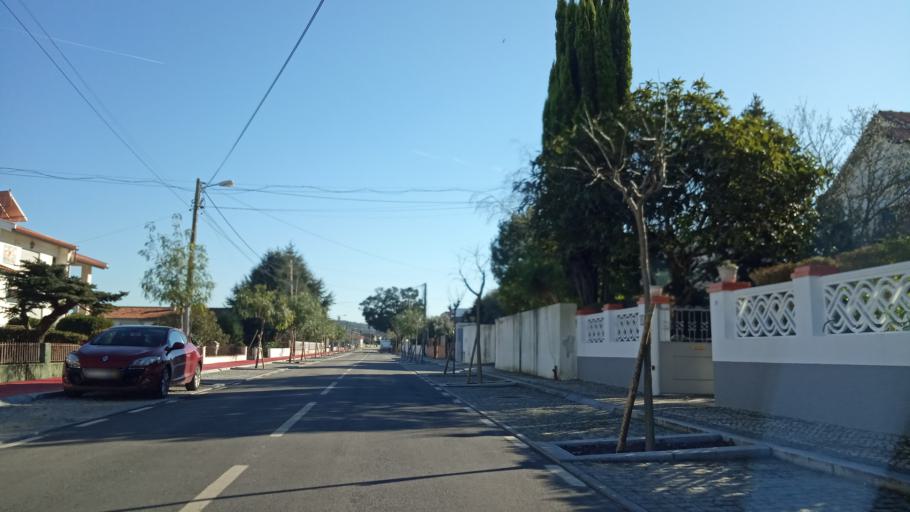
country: PT
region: Aveiro
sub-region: Anadia
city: Anadia
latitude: 40.4325
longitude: -8.4312
